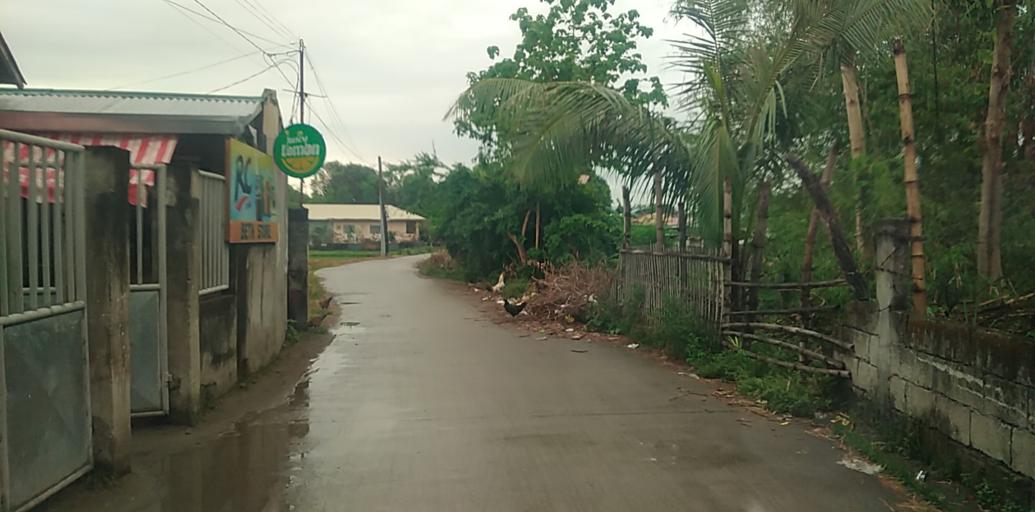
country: PH
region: Central Luzon
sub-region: Province of Pampanga
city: Anao
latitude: 15.1456
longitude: 120.7247
